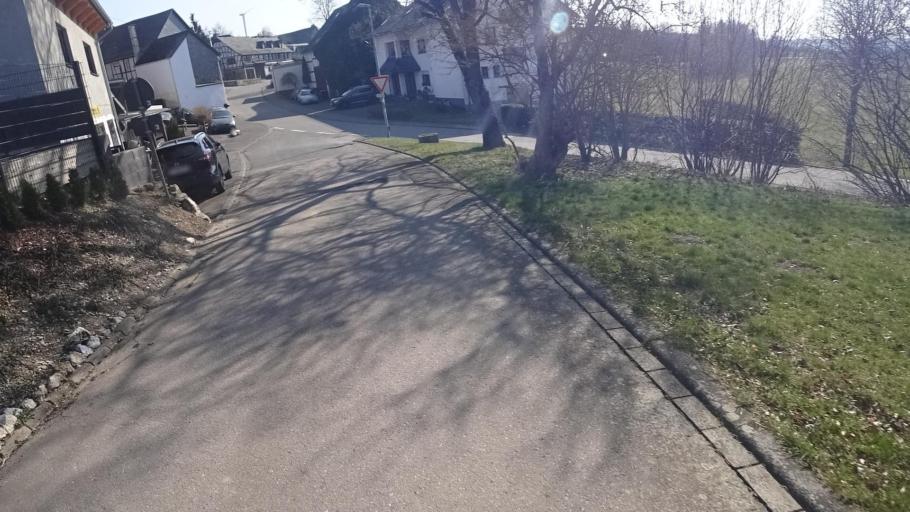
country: DE
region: Rheinland-Pfalz
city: Riegenroth
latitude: 50.0450
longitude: 7.5945
